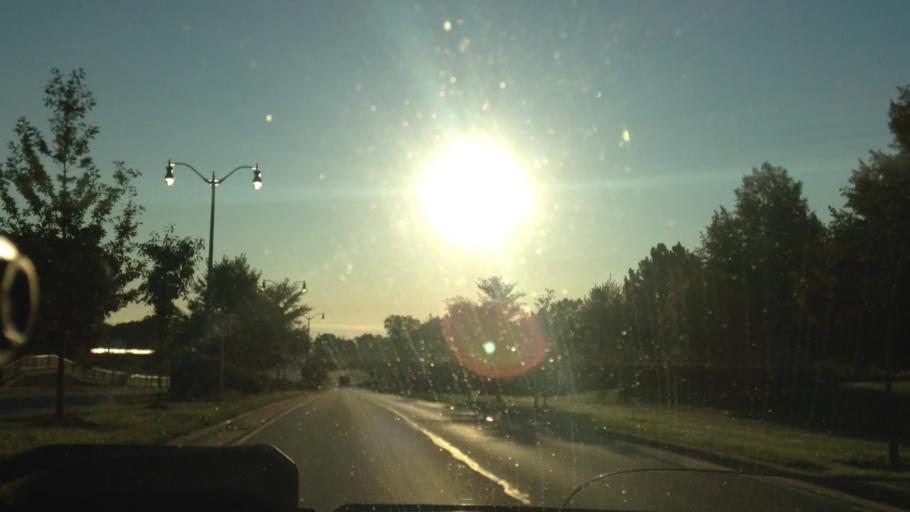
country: US
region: Wisconsin
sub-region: Ozaukee County
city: Port Washington
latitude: 43.3869
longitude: -87.9046
